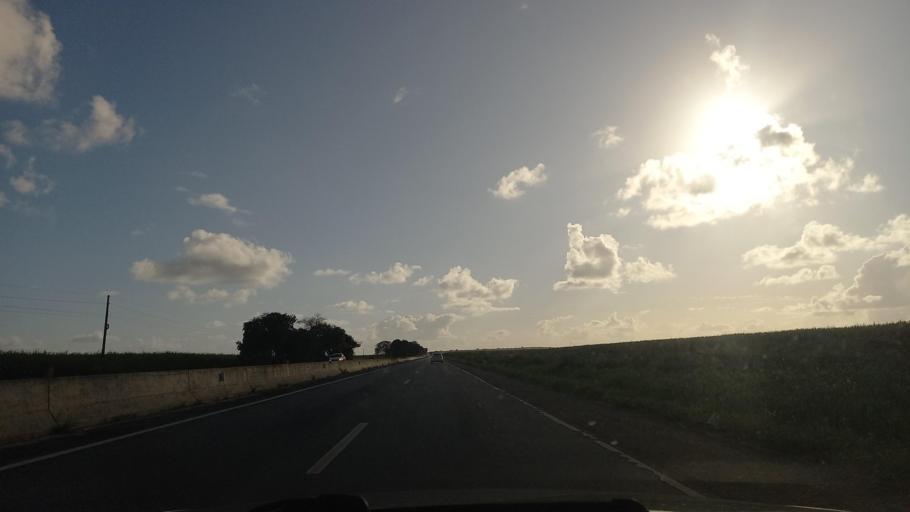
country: BR
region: Alagoas
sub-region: Sao Miguel Dos Campos
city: Sao Miguel dos Campos
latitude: -9.7997
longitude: -36.1675
